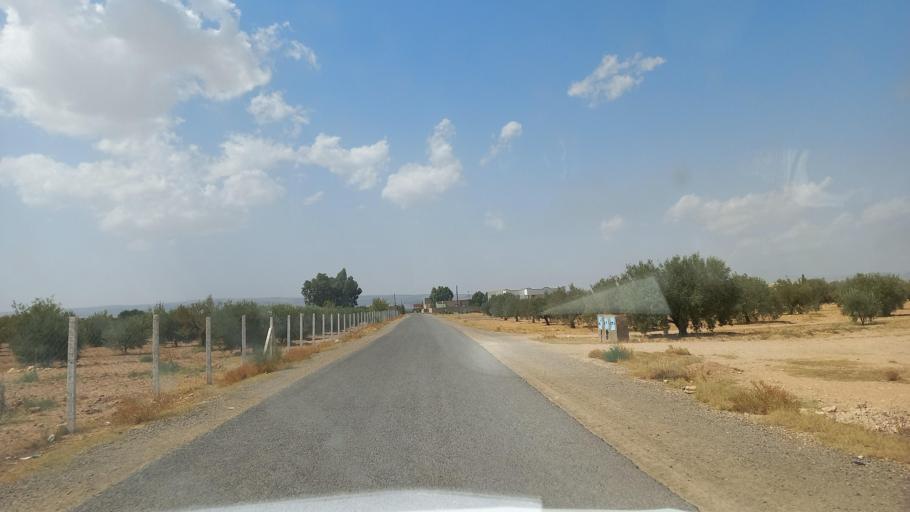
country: TN
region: Al Qasrayn
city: Kasserine
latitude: 35.2499
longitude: 9.0205
